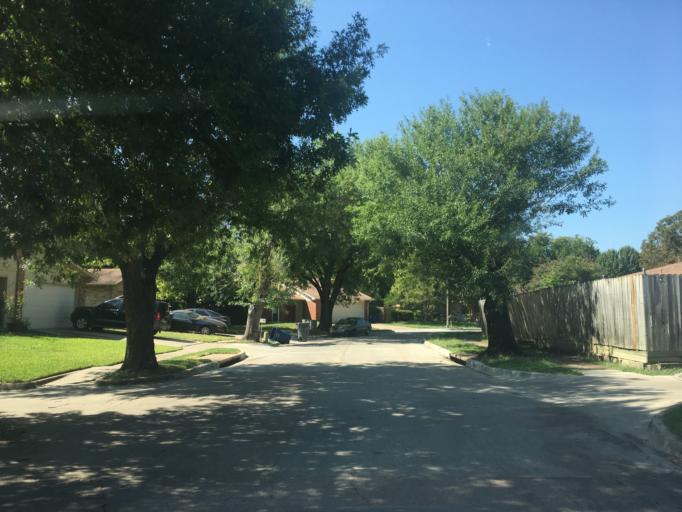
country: US
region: Texas
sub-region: Dallas County
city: Garland
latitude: 32.8551
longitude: -96.6542
